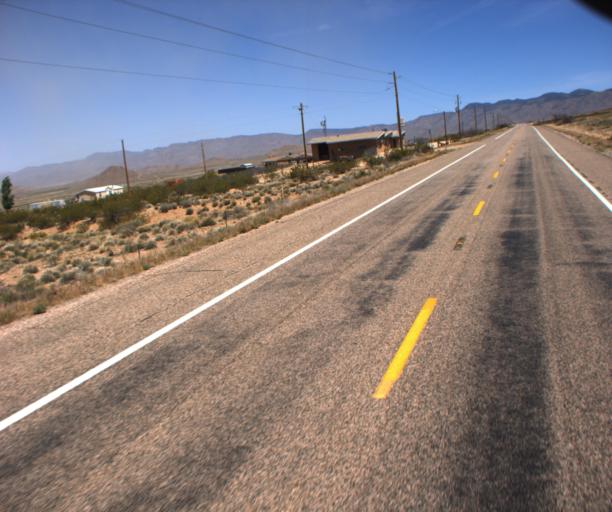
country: US
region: Arizona
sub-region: Mohave County
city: New Kingman-Butler
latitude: 35.3970
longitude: -113.8386
